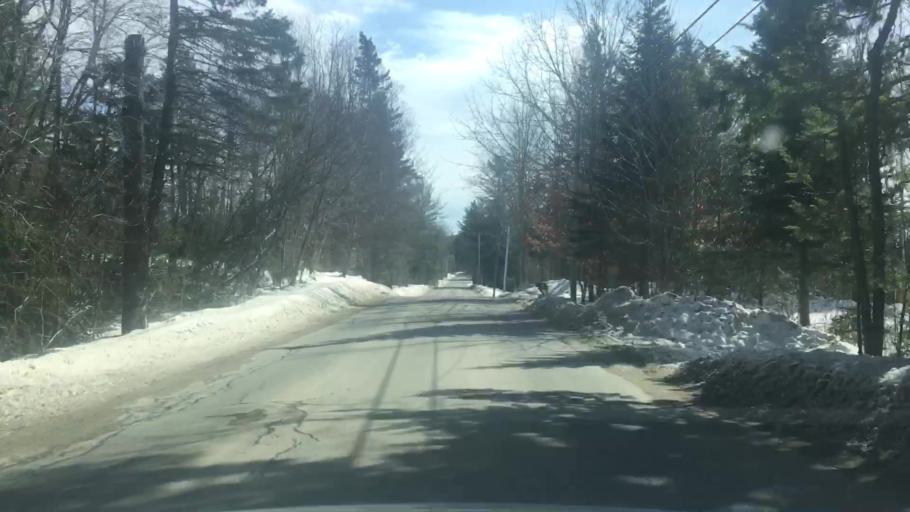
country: US
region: Maine
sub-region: Penobscot County
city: Holden
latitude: 44.7572
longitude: -68.6383
